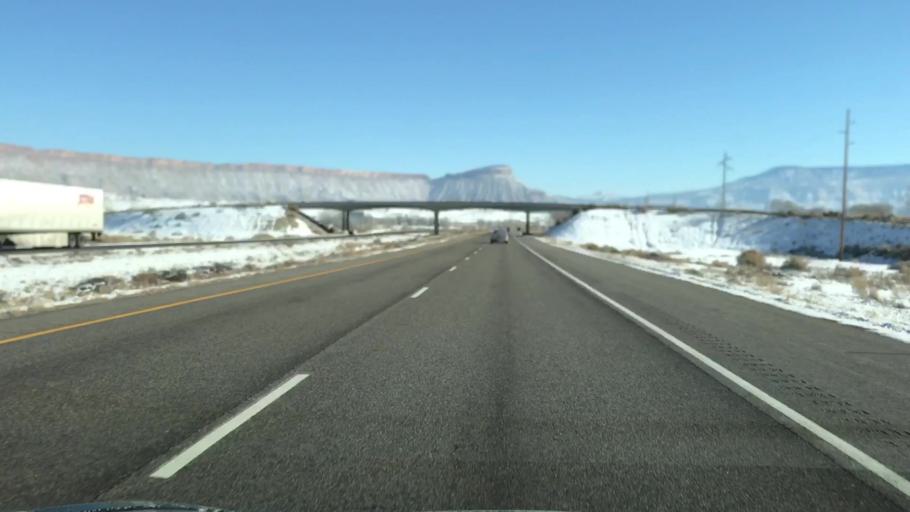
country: US
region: Colorado
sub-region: Mesa County
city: Fruitvale
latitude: 39.1077
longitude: -108.5131
